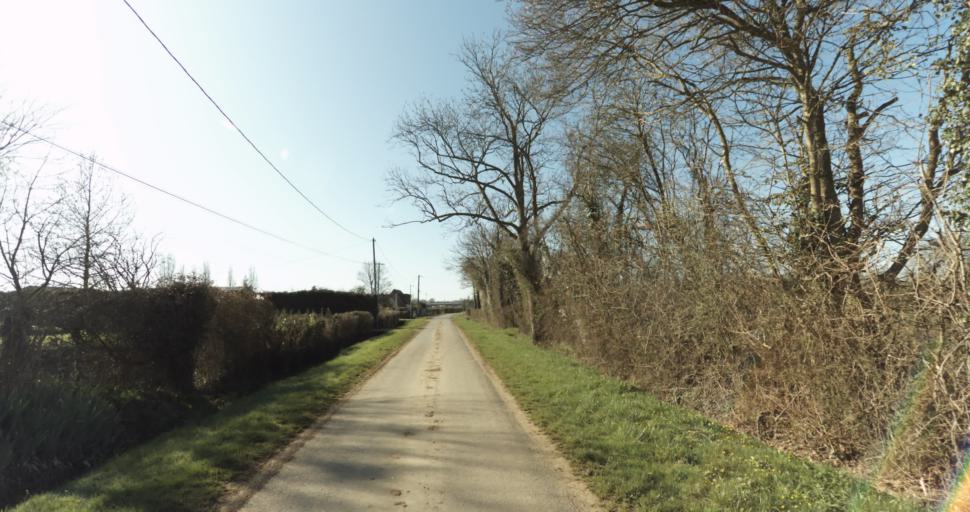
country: FR
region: Lower Normandy
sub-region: Departement du Calvados
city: Saint-Pierre-sur-Dives
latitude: 48.9727
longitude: 0.0212
